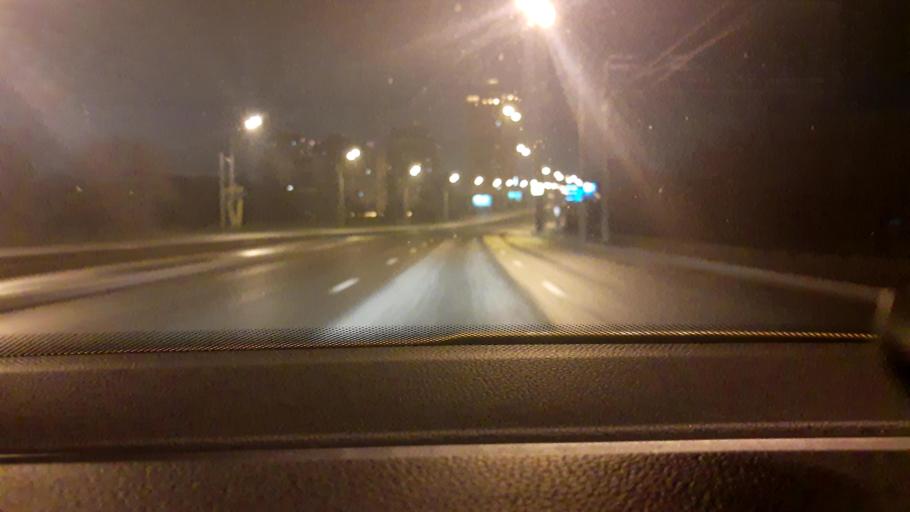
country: RU
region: Moscow
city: Shchukino
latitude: 55.8040
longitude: 37.4333
